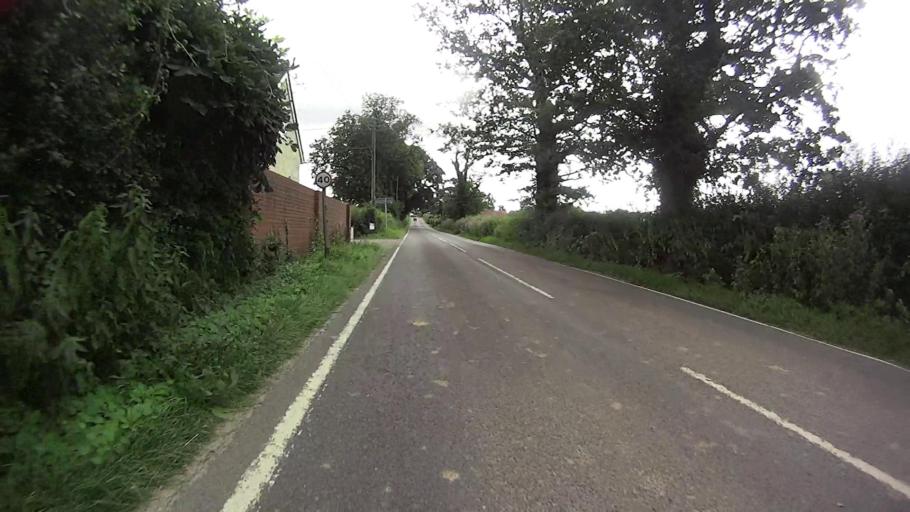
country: GB
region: England
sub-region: Surrey
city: Reigate
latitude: 51.1830
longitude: -0.2317
